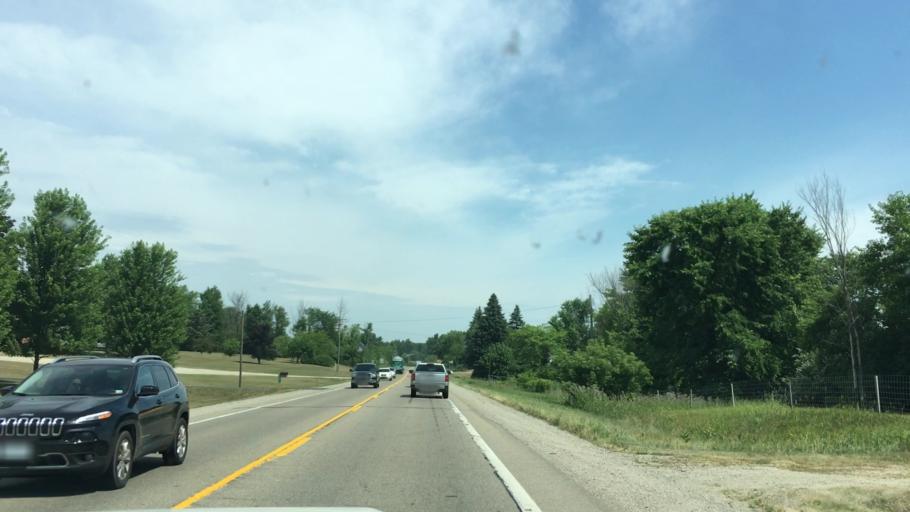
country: US
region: Michigan
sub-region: Lapeer County
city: Imlay City
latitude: 43.0779
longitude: -83.0755
